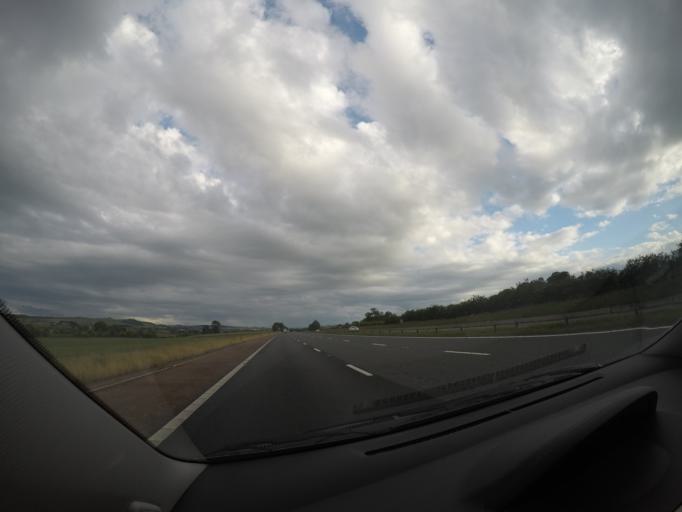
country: GB
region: England
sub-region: Cumbria
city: Penrith
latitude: 54.7376
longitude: -2.8063
